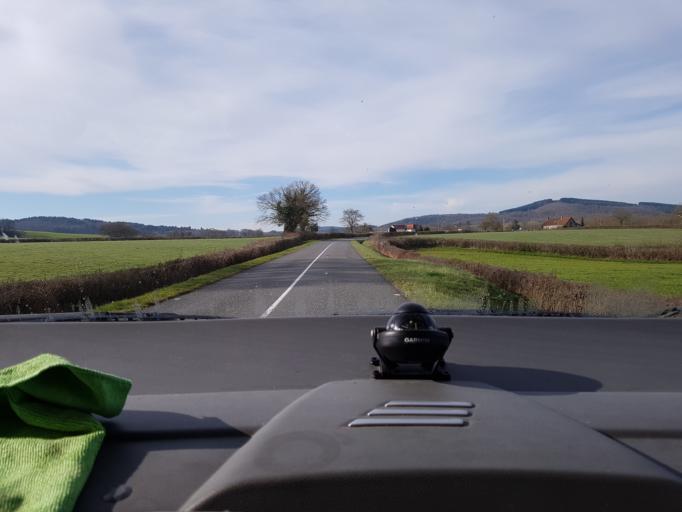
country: FR
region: Bourgogne
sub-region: Departement de Saone-et-Loire
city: Toulon-sur-Arroux
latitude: 46.7555
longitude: 4.1349
